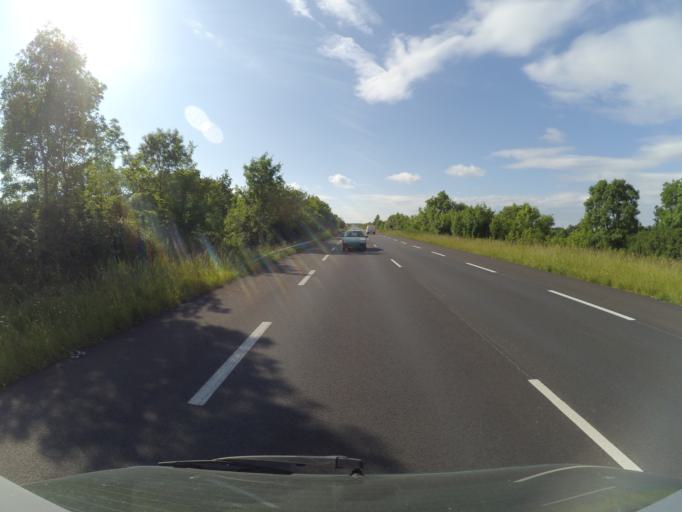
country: FR
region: Poitou-Charentes
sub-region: Departement de la Charente-Maritime
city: Saint-Agnant
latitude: 45.8415
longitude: -0.9473
